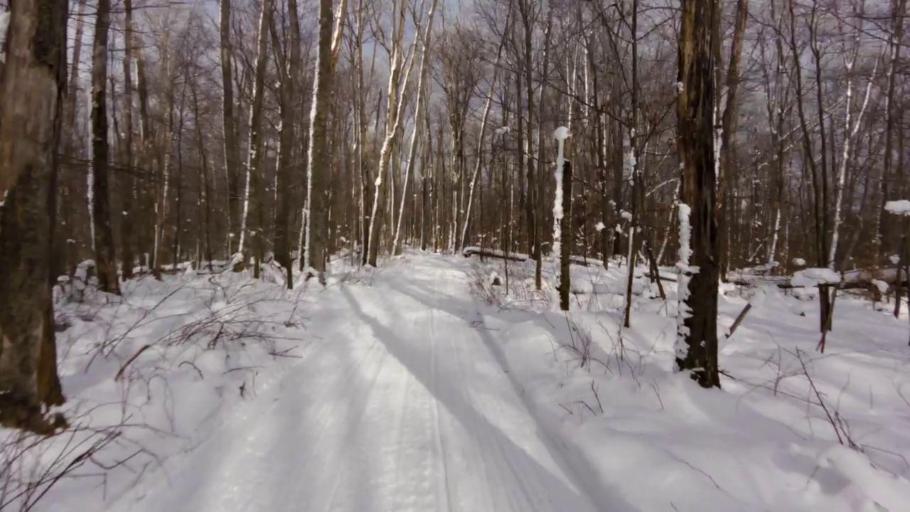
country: US
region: New York
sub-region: Cattaraugus County
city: Salamanca
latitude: 42.0376
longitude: -78.7535
